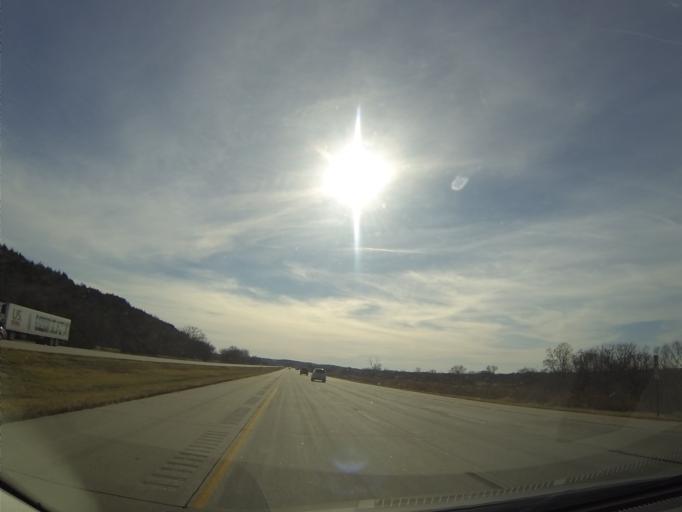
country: US
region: Nebraska
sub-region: Saunders County
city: Ashland
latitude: 41.0478
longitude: -96.2956
